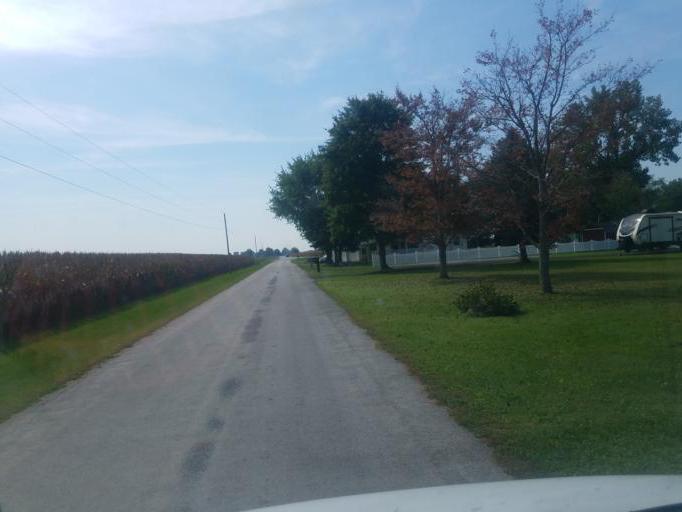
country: US
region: Ohio
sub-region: Marion County
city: Marion
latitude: 40.6712
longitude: -83.1447
